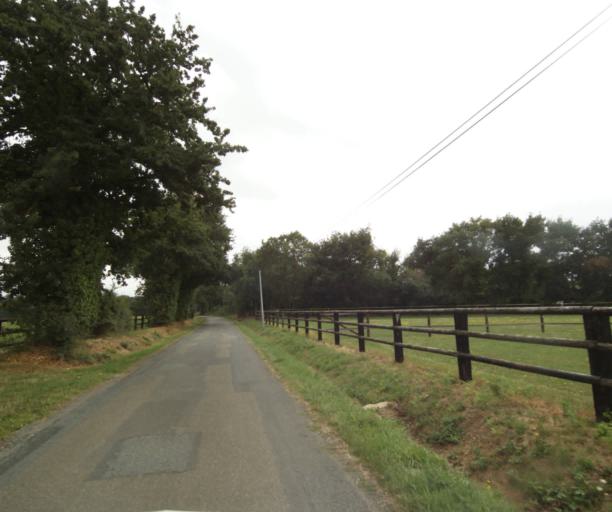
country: FR
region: Pays de la Loire
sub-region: Departement de la Sarthe
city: Solesmes
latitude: 47.8416
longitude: -0.2723
